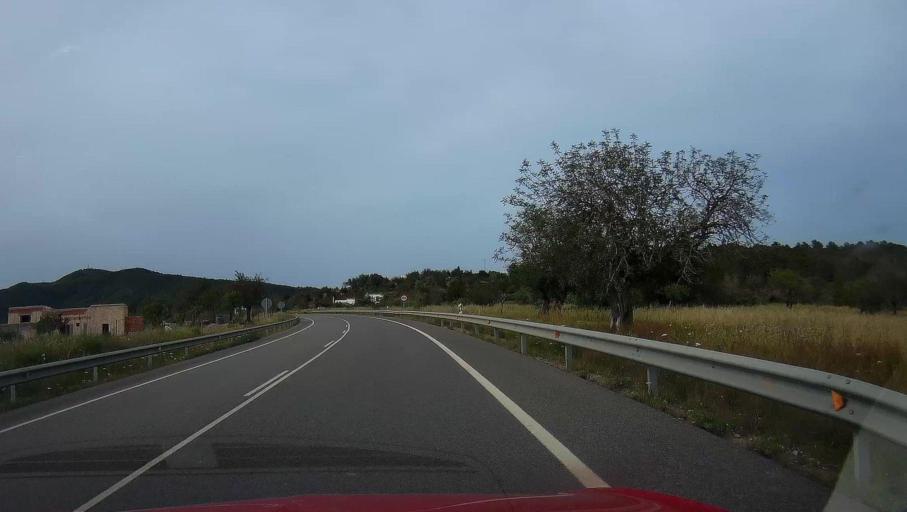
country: ES
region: Balearic Islands
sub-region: Illes Balears
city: Sant Joan de Labritja
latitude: 39.0614
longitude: 1.4947
